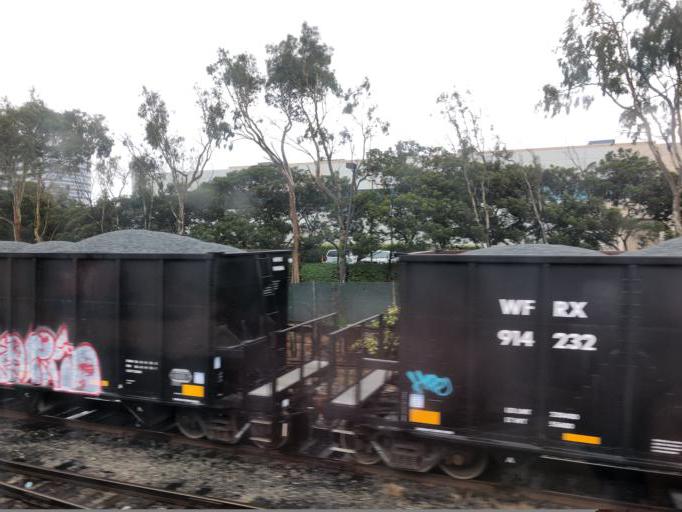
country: US
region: California
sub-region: San Mateo County
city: South San Francisco
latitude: 37.6575
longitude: -122.4034
